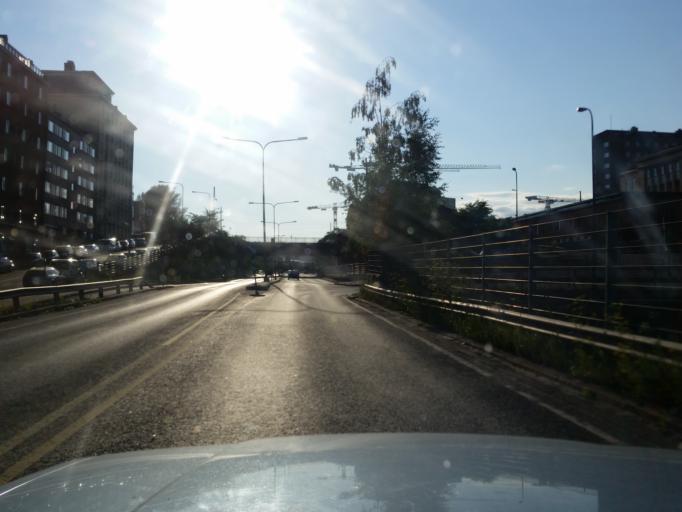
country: FI
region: Uusimaa
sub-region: Helsinki
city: Helsinki
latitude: 60.1890
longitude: 24.9671
